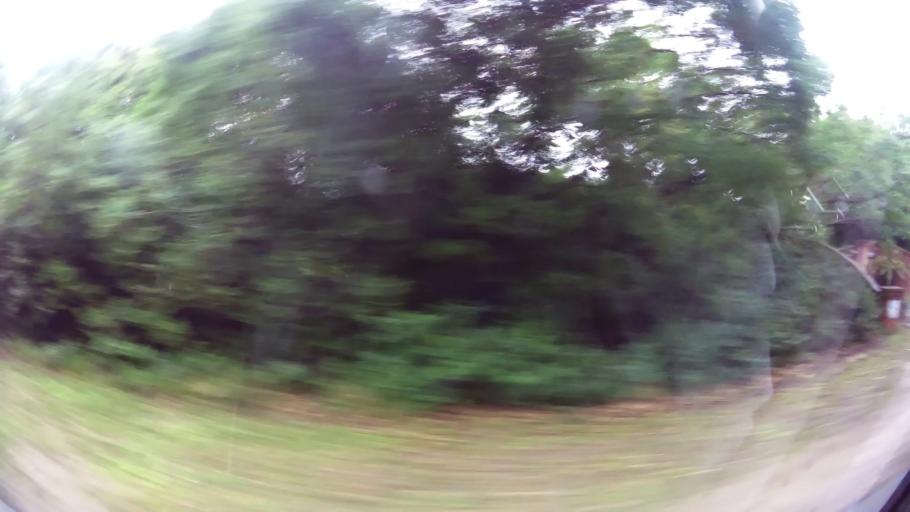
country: ZA
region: Eastern Cape
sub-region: Nelson Mandela Bay Metropolitan Municipality
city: Port Elizabeth
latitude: -34.0159
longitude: 25.5113
